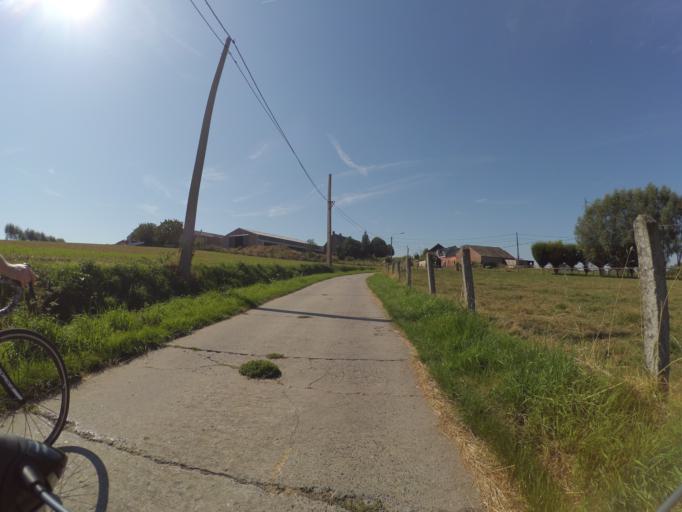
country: BE
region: Flanders
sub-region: Provincie Oost-Vlaanderen
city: Ronse
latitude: 50.7823
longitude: 3.6087
